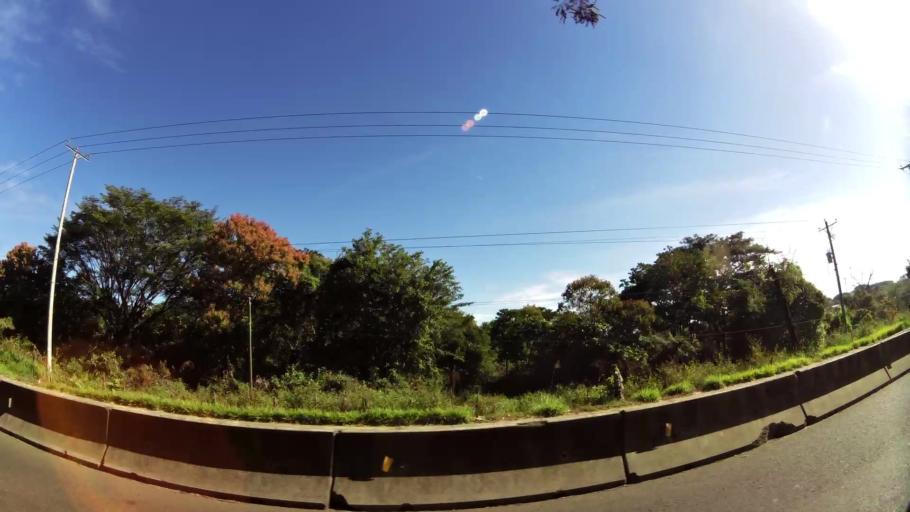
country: SV
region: Santa Ana
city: Santa Ana
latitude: 13.9568
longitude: -89.5760
